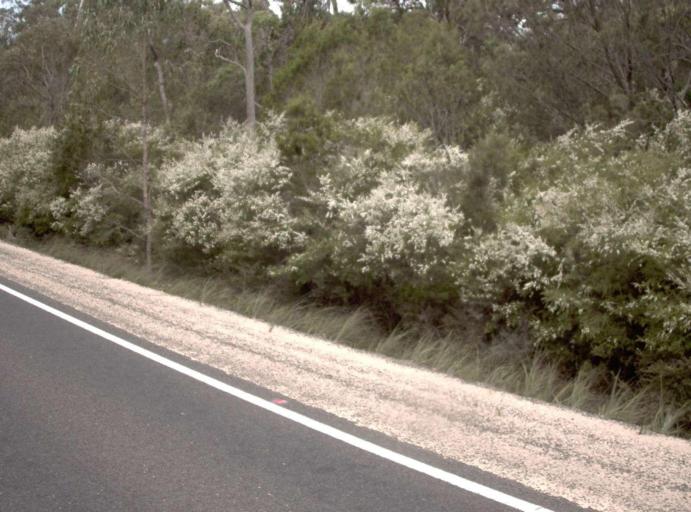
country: AU
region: New South Wales
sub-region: Bega Valley
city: Eden
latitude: -37.4459
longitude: 149.6299
